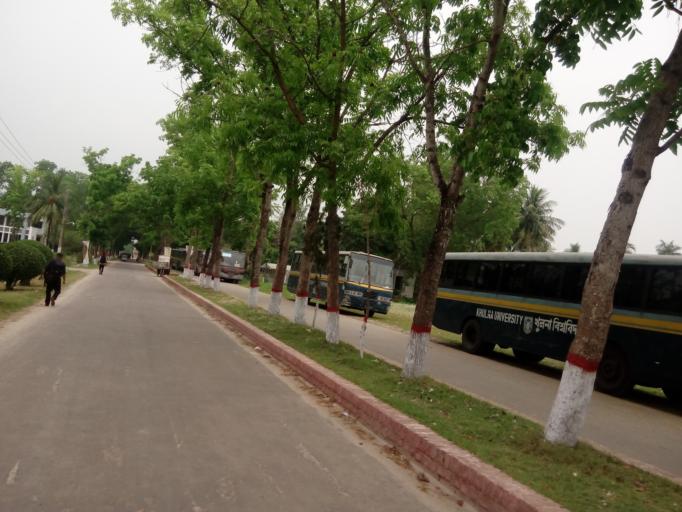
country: BD
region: Khulna
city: Khulna
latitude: 22.7998
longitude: 89.5345
